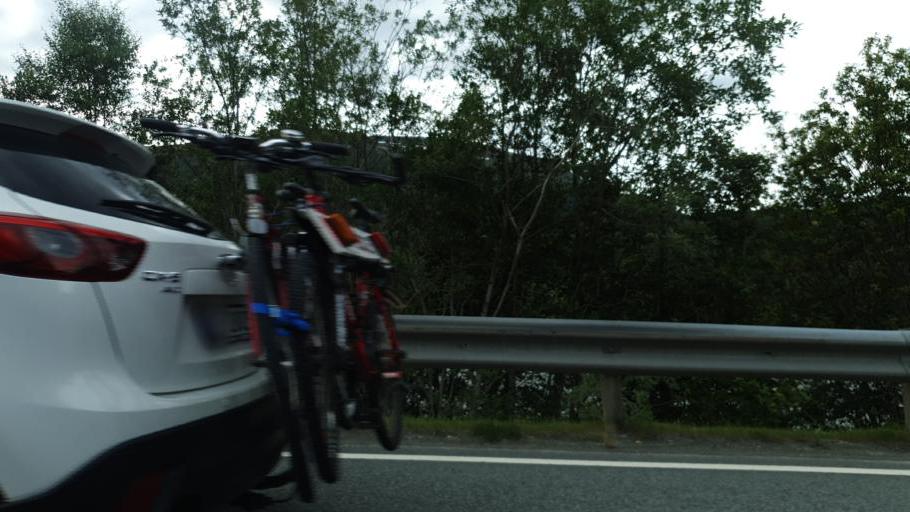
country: NO
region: Sor-Trondelag
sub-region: Oppdal
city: Oppdal
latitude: 62.5530
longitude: 9.6326
